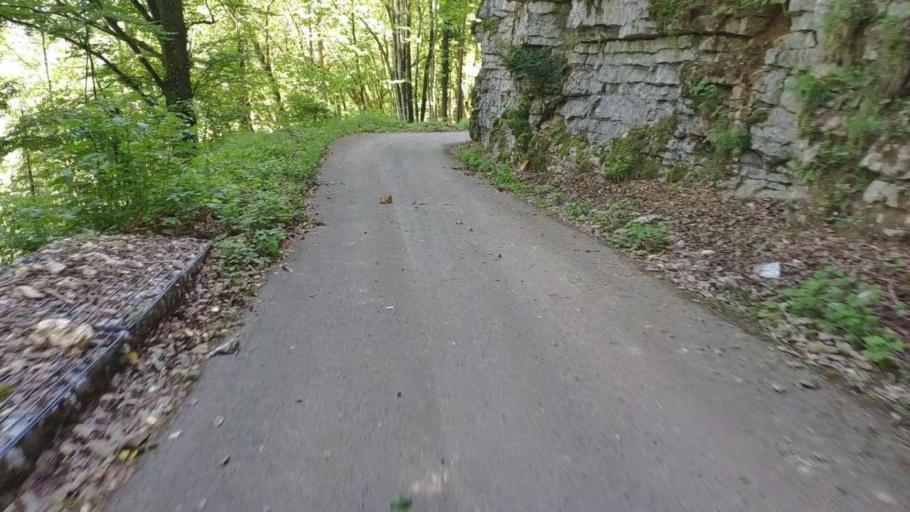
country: FR
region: Franche-Comte
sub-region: Departement du Jura
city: Poligny
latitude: 46.7458
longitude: 5.6761
